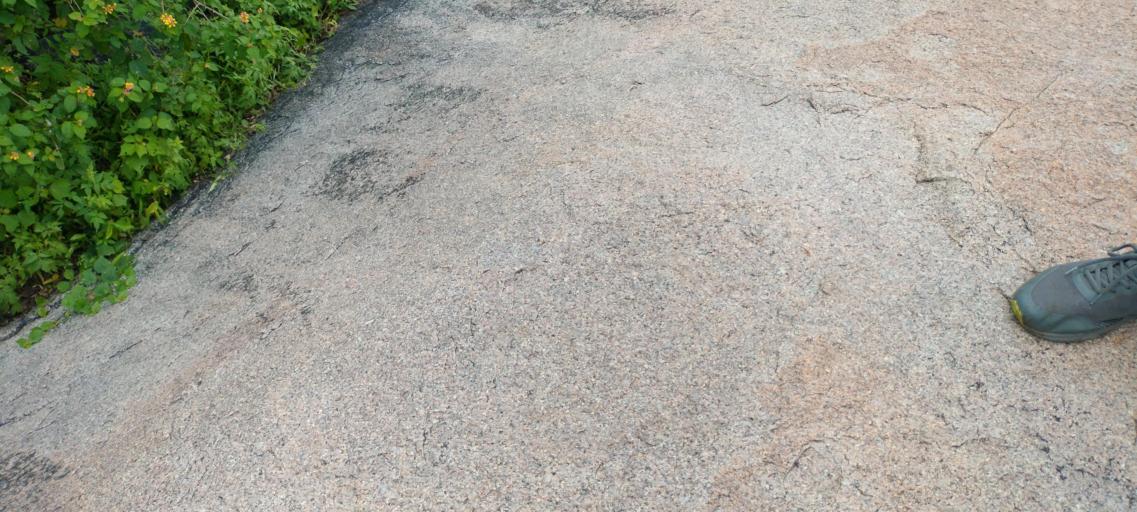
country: IN
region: Telangana
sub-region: Mahbubnagar
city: Farrukhnagar
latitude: 16.8948
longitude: 78.4926
